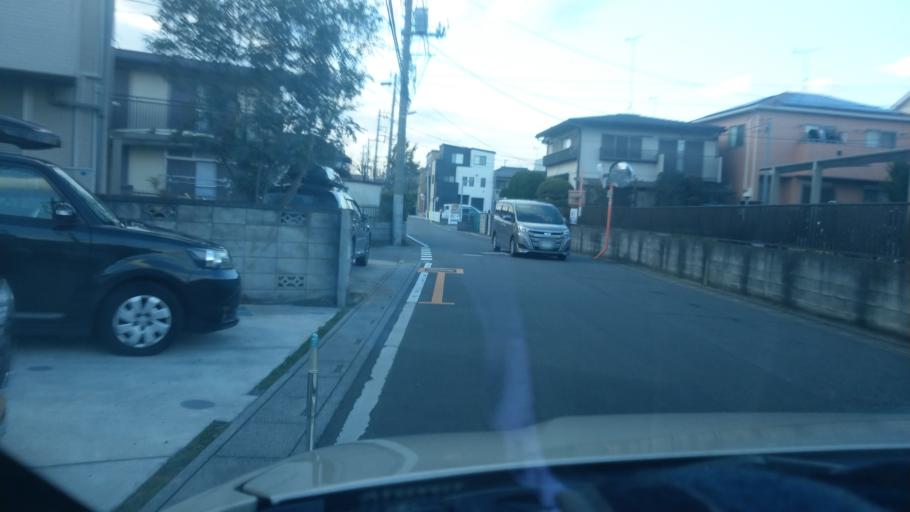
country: JP
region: Saitama
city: Yono
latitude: 35.8902
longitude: 139.6031
